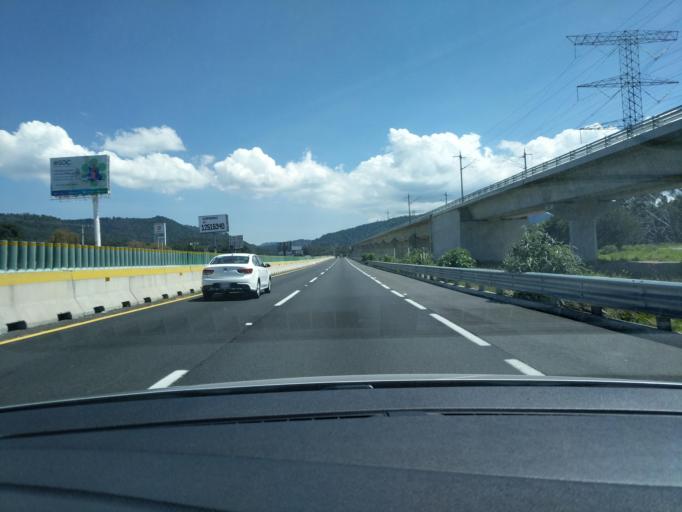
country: MX
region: Morelos
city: Ocoyoacac
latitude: 19.2863
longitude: -99.4439
